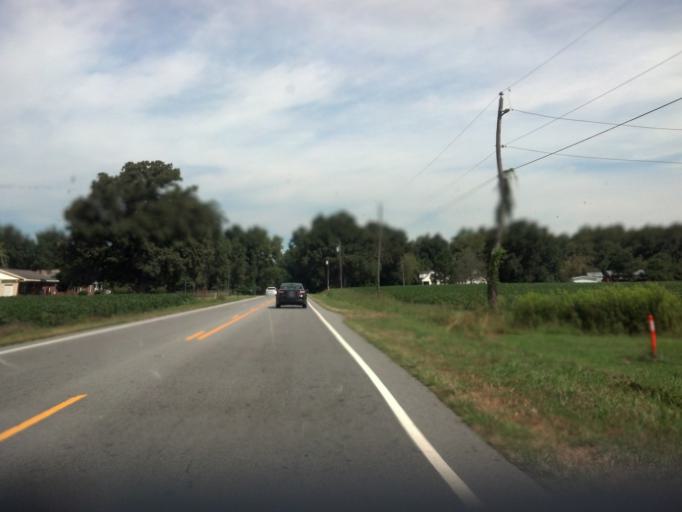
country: US
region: North Carolina
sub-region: Greene County
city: Maury
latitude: 35.5121
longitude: -77.6171
